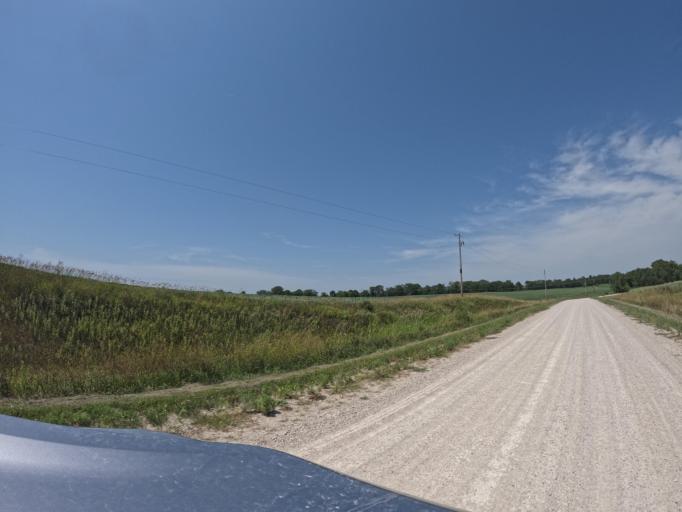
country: US
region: Iowa
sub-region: Henry County
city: Mount Pleasant
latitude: 40.9763
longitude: -91.6598
